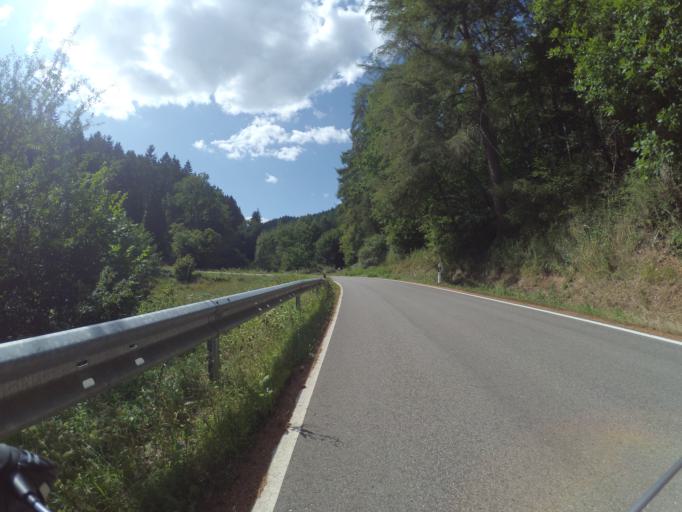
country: DE
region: Rheinland-Pfalz
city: Budlich
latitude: 49.7697
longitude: 6.8877
